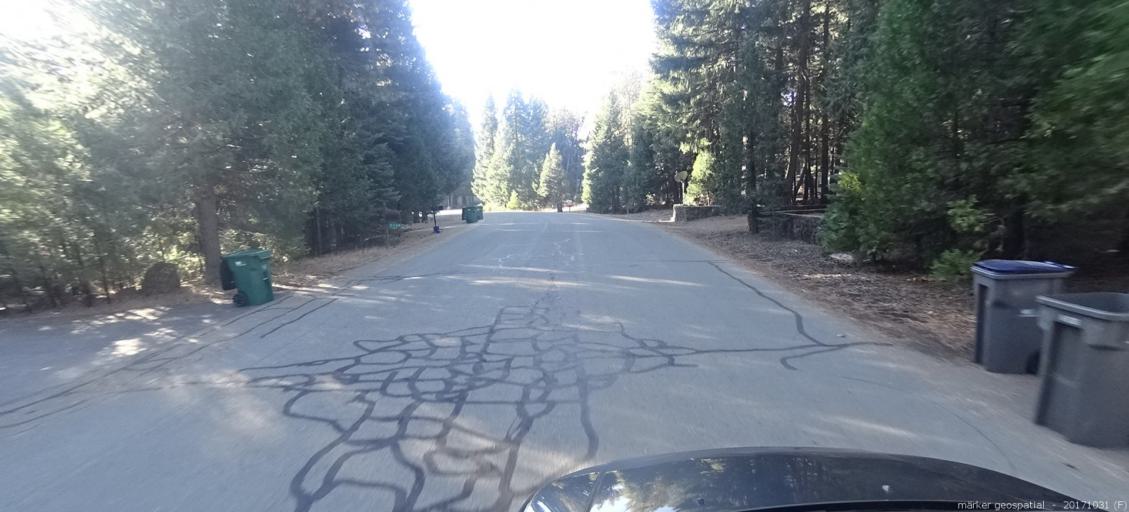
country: US
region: California
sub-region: Shasta County
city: Shingletown
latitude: 40.5241
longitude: -121.7950
